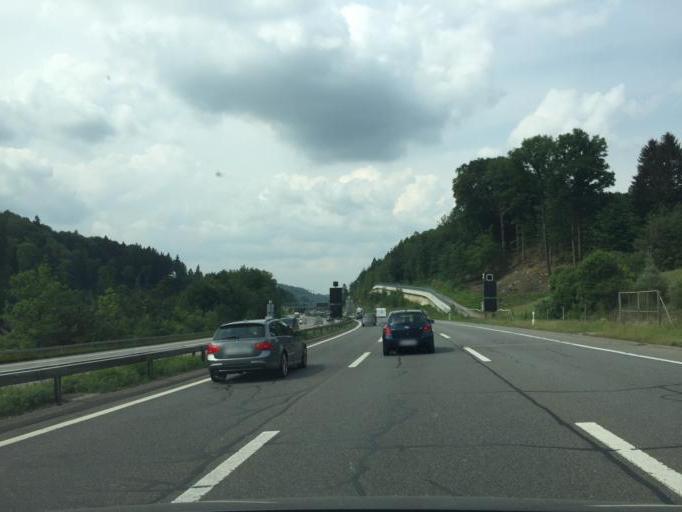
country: CH
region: Zurich
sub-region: Bezirk Winterthur
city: Toss
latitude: 47.4606
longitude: 8.7092
